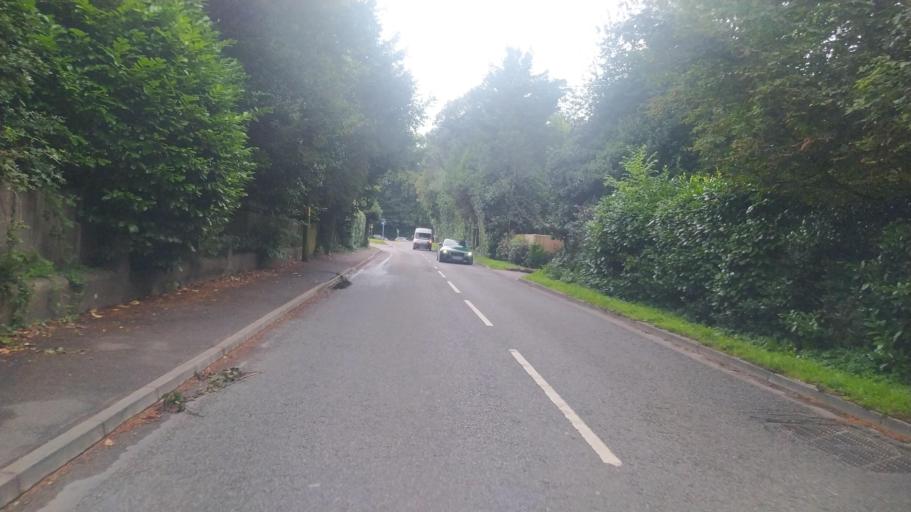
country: GB
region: England
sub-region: Hampshire
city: Liss
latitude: 51.0317
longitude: -0.8772
